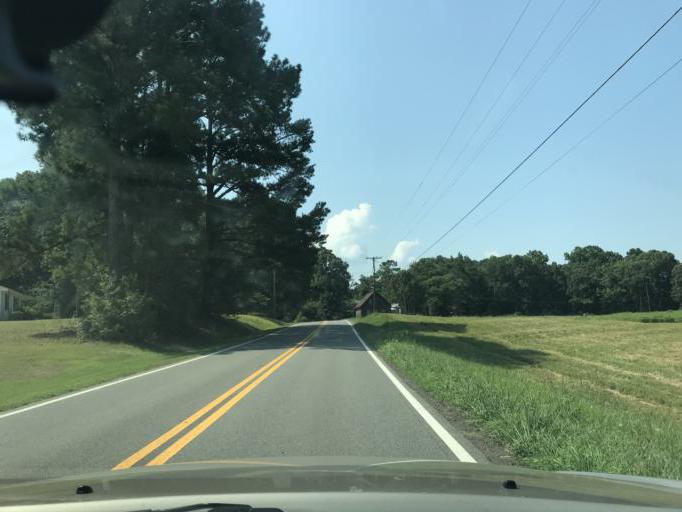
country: US
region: Georgia
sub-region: Hall County
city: Flowery Branch
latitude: 34.2382
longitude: -83.9976
